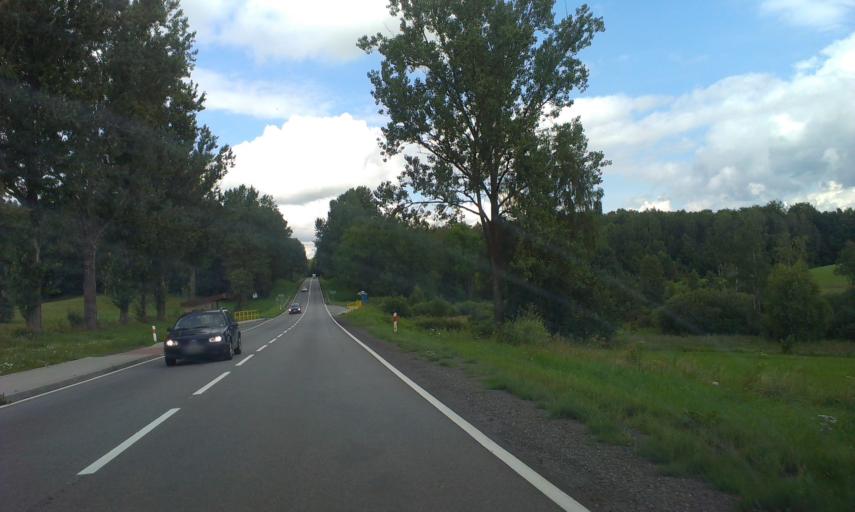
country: PL
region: West Pomeranian Voivodeship
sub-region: Powiat koszalinski
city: Bobolice
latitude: 53.9130
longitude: 16.6078
